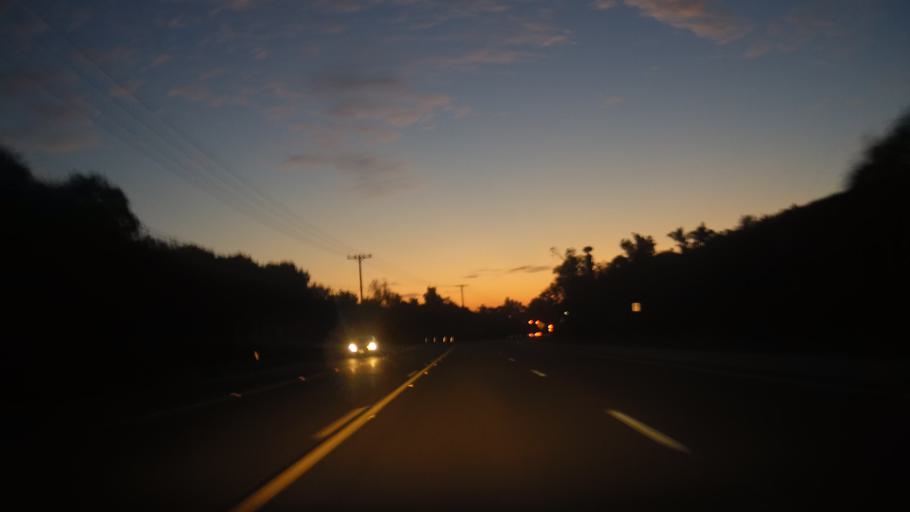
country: US
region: California
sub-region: San Diego County
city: Rancho San Diego
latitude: 32.7470
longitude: -116.9137
